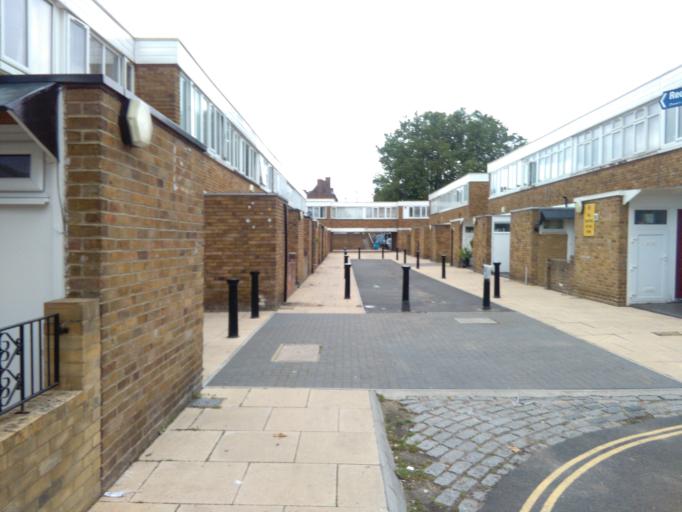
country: GB
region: England
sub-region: Greater London
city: Kennington
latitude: 51.4814
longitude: -0.1177
